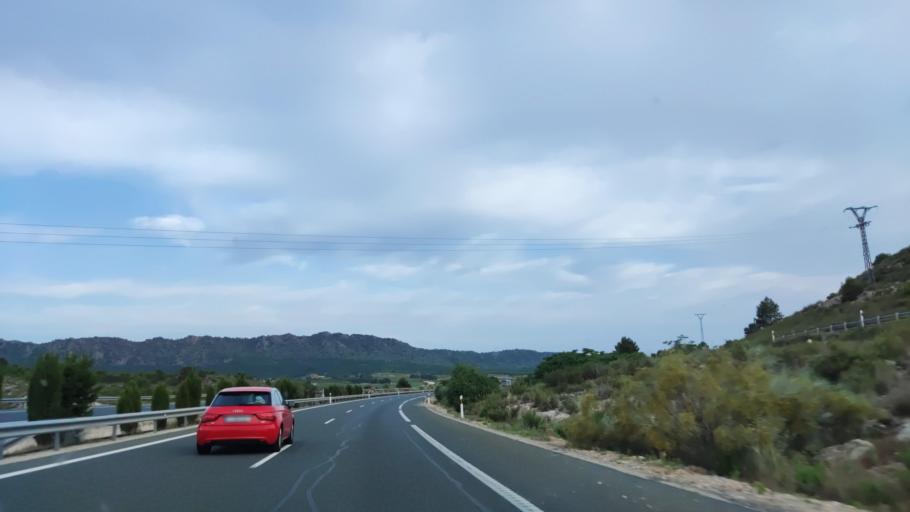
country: ES
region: Castille-La Mancha
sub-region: Provincia de Albacete
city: Tobarra
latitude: 38.6703
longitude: -1.6660
